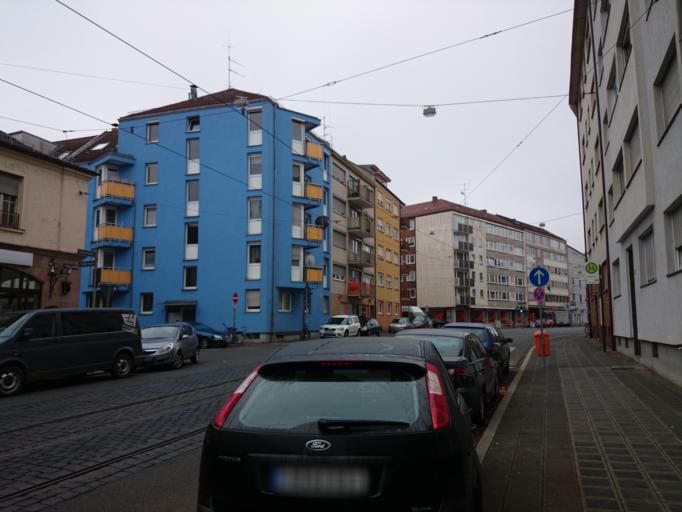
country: DE
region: Bavaria
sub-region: Regierungsbezirk Mittelfranken
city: Nuernberg
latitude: 49.4454
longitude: 11.0892
